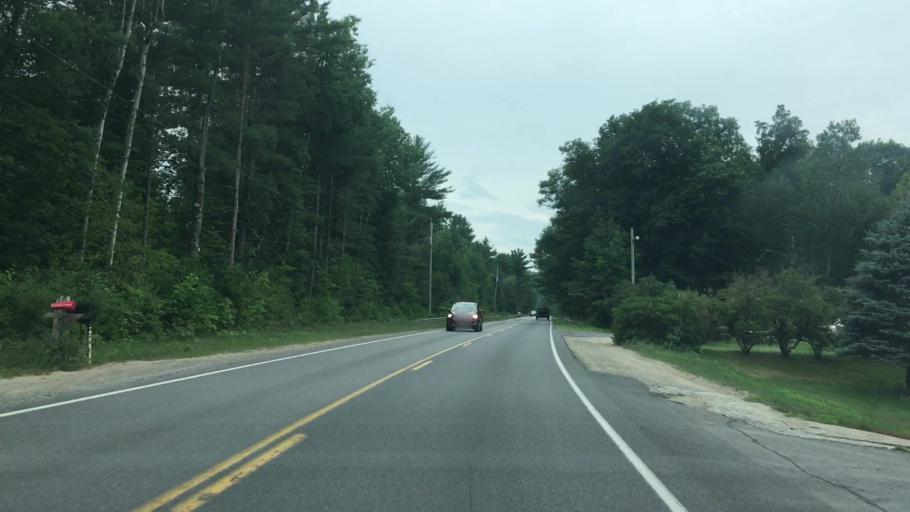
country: US
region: New York
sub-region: Clinton County
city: Peru
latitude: 44.5071
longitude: -73.5845
